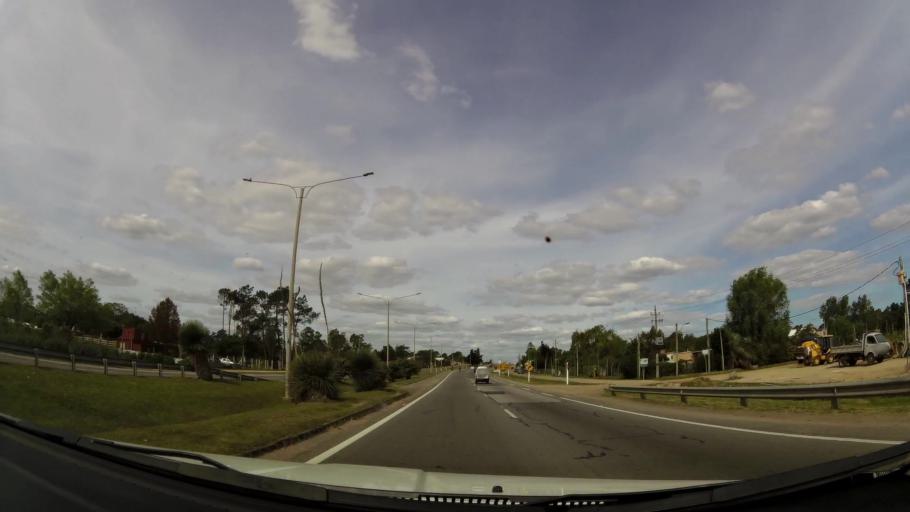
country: UY
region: Canelones
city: Empalme Olmos
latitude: -34.7796
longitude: -55.8692
